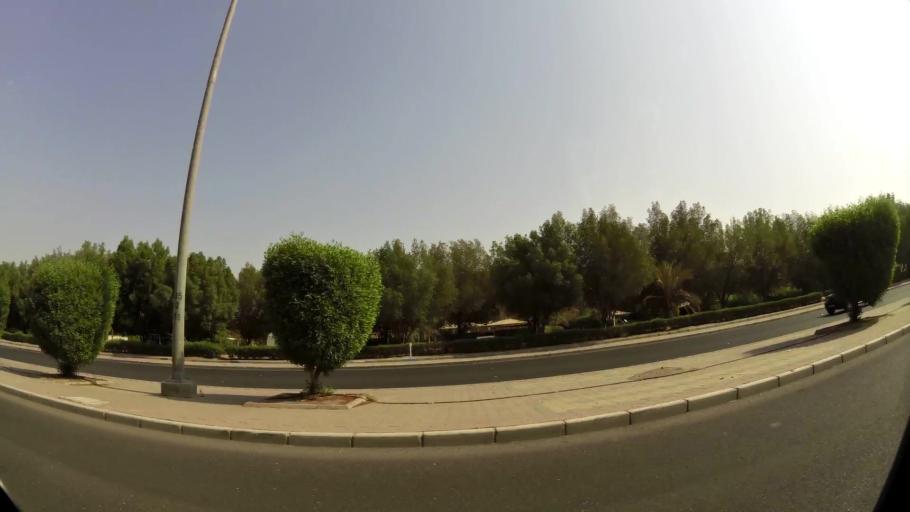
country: KW
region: Al Asimah
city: Ar Rabiyah
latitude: 29.2834
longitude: 47.8854
